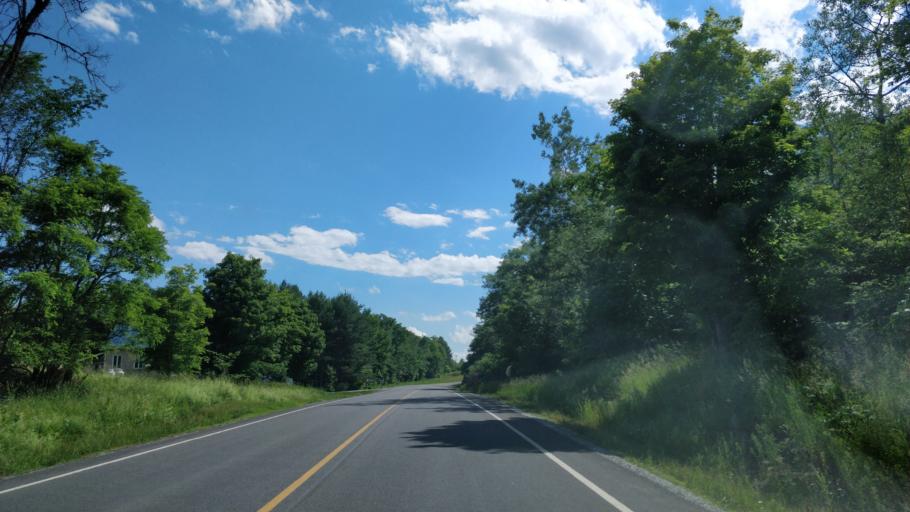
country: CA
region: Ontario
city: Perth
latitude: 44.7790
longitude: -76.4488
